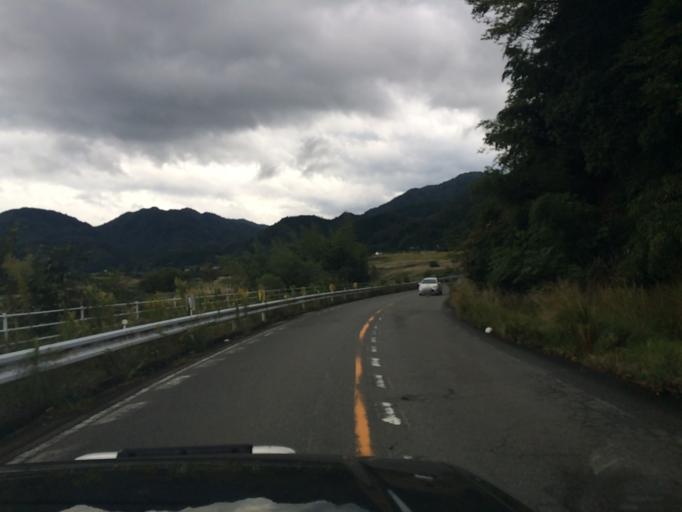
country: JP
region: Hyogo
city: Toyooka
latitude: 35.4525
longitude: 134.7739
